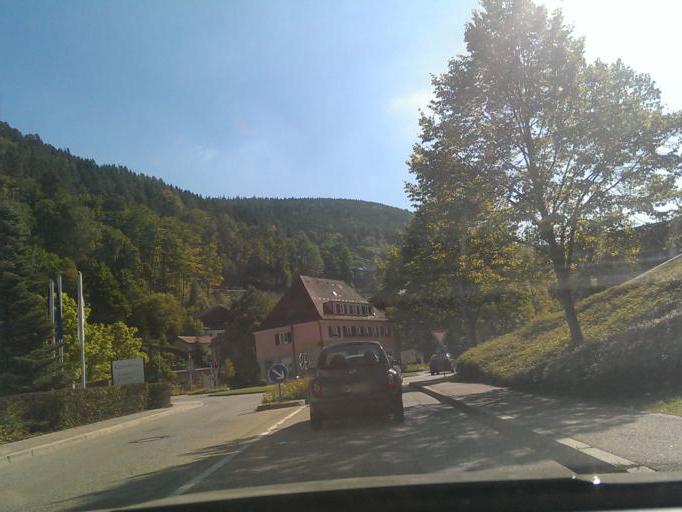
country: DE
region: Baden-Wuerttemberg
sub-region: Karlsruhe Region
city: Bad Wildbad
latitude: 48.7567
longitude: 8.5523
